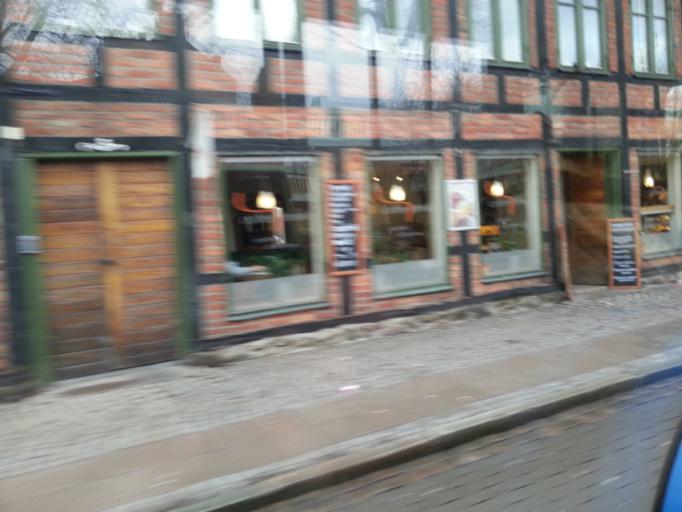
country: SE
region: Skane
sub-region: Lunds Kommun
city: Lund
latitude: 55.7062
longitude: 13.1924
